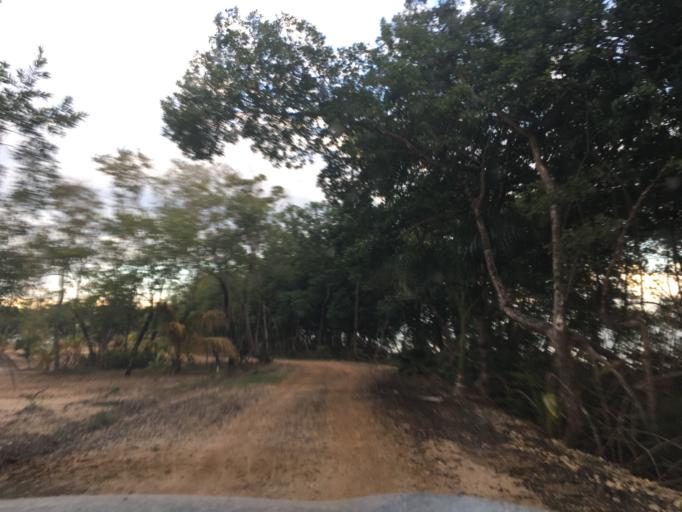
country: BZ
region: Stann Creek
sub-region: Dangriga
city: Dangriga
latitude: 16.8343
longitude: -88.2635
